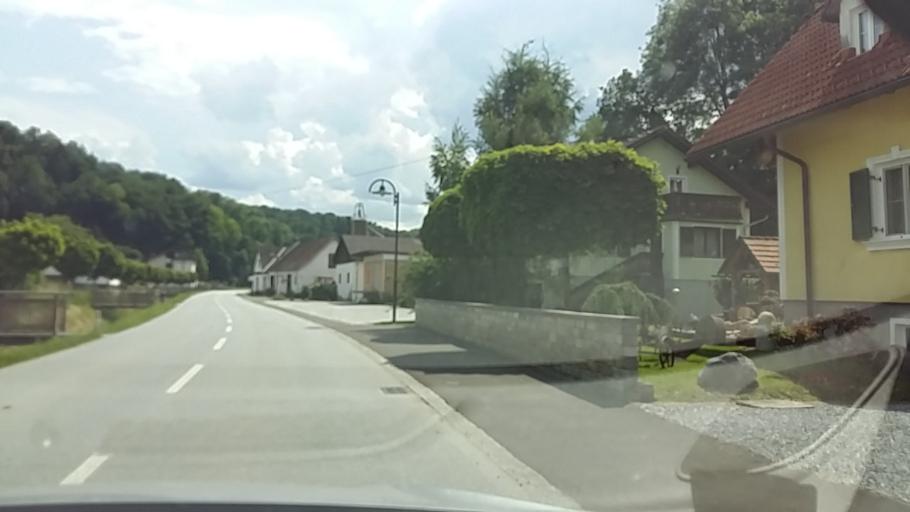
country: AT
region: Styria
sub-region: Politischer Bezirk Suedoststeiermark
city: Breitenfeld an der Rittschein
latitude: 47.0334
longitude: 15.9600
